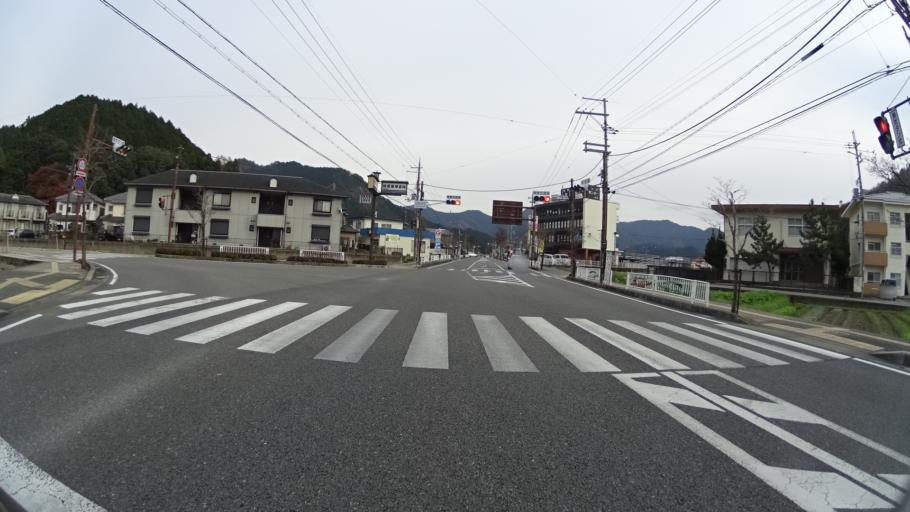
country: JP
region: Hyogo
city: Sasayama
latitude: 35.1252
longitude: 135.0819
